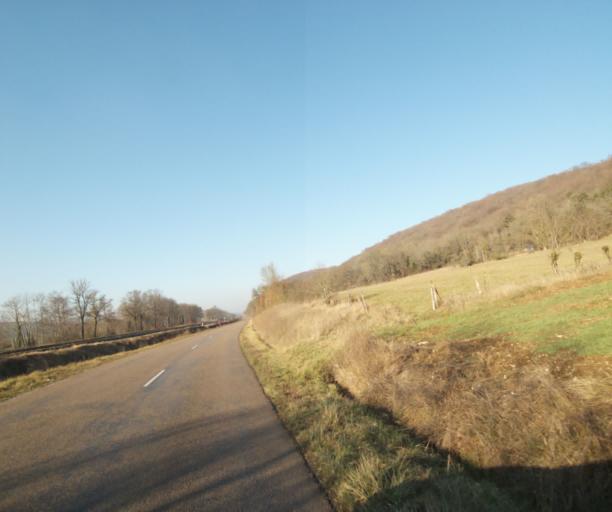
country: FR
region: Champagne-Ardenne
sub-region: Departement de la Haute-Marne
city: Chevillon
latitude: 48.5025
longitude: 5.1276
